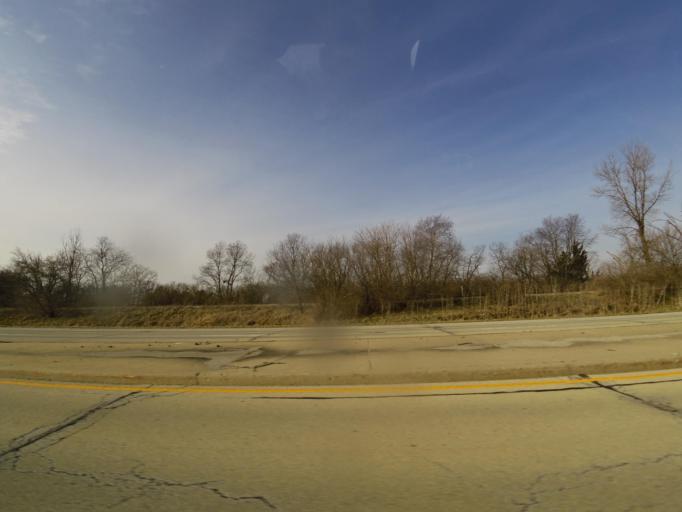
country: US
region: Illinois
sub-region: Macon County
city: Decatur
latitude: 39.7841
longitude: -88.9783
